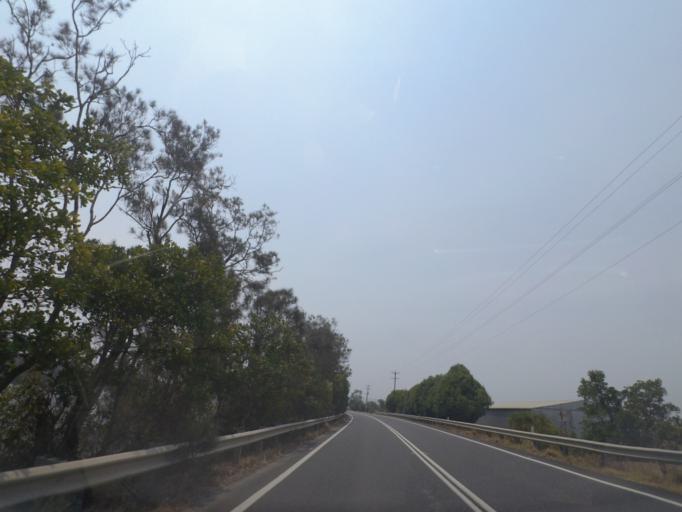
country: AU
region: New South Wales
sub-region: Richmond Valley
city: Evans Head
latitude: -28.9793
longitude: 153.4622
